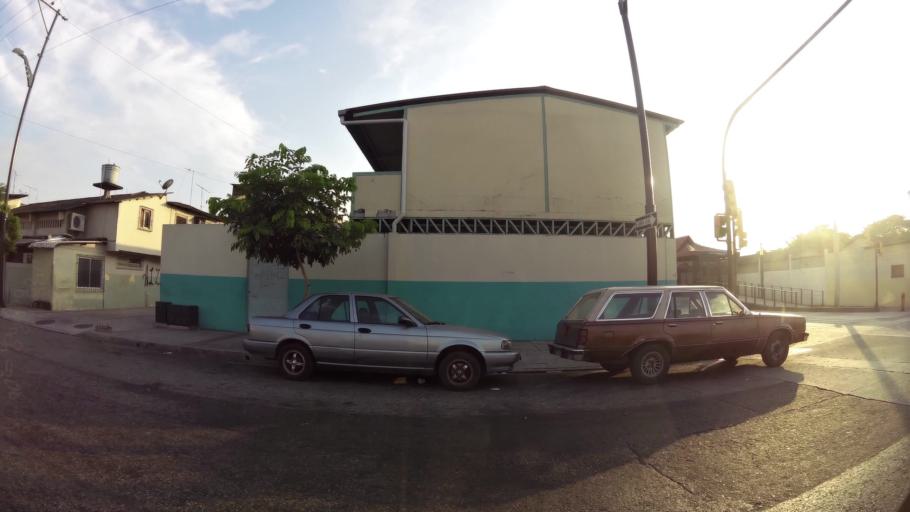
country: EC
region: Guayas
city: Guayaquil
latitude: -2.2124
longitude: -79.8972
